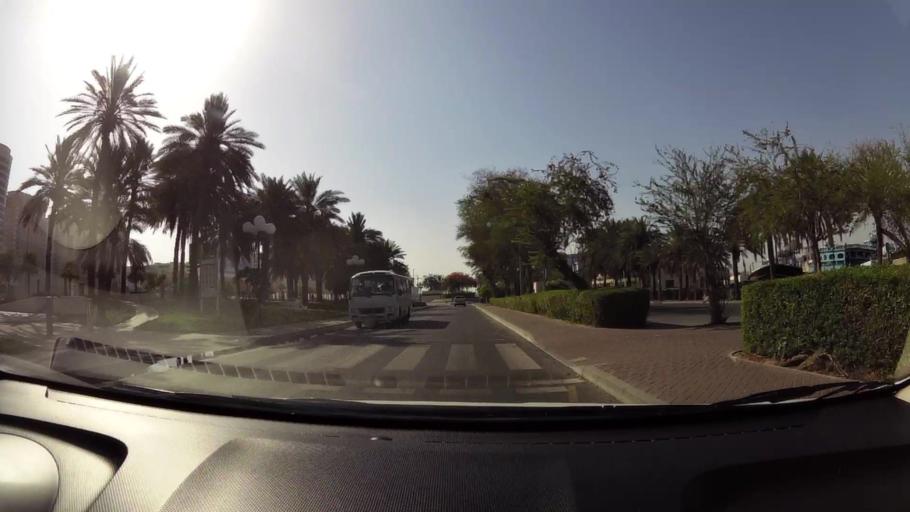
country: AE
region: Ash Shariqah
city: Sharjah
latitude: 25.2569
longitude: 55.3210
